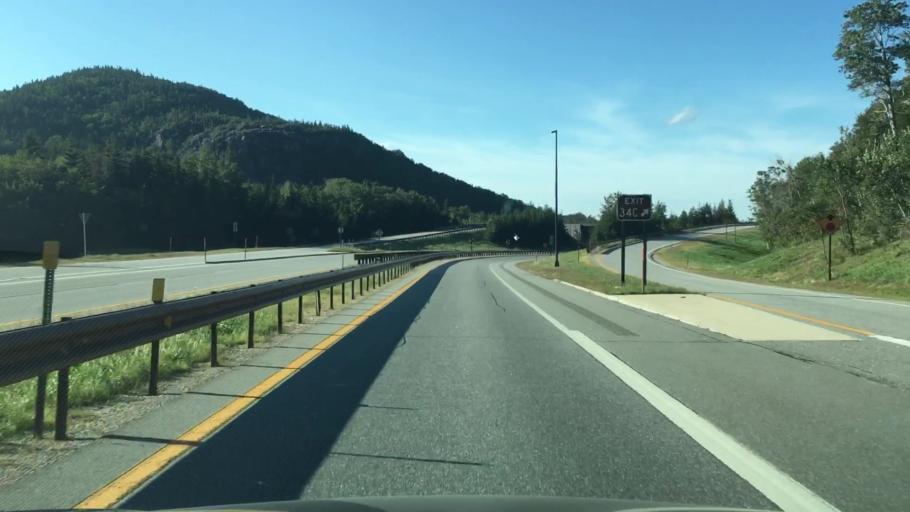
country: US
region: New Hampshire
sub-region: Grafton County
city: Deerfield
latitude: 44.1771
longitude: -71.6910
